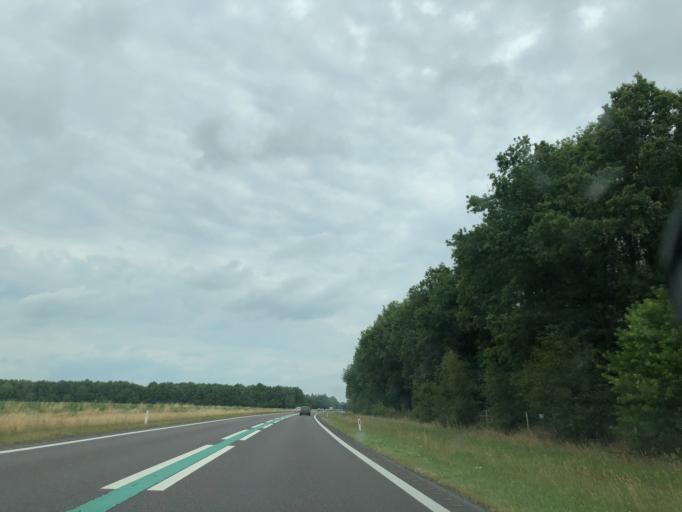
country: NL
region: Drenthe
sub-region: Gemeente Aa en Hunze
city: Anloo
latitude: 53.0598
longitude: 6.7049
